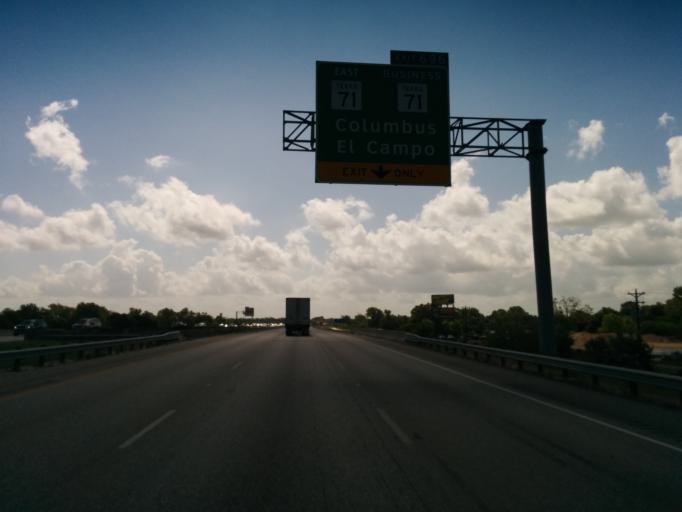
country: US
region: Texas
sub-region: Colorado County
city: Columbus
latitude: 29.6929
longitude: -96.5537
